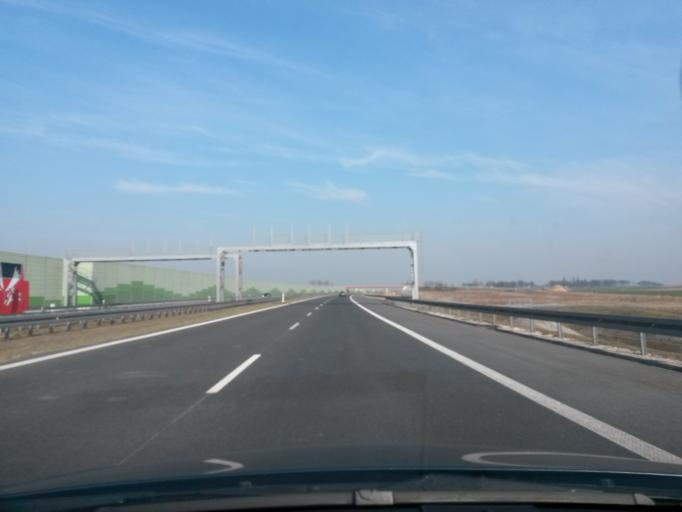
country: PL
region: Lodz Voivodeship
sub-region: Powiat kutnowski
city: Krzyzanow
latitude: 52.1421
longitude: 19.4829
